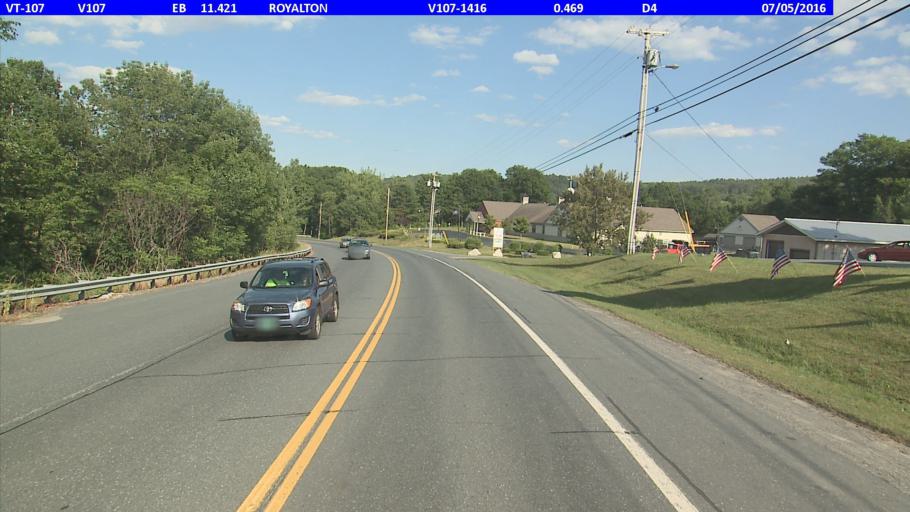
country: US
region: Vermont
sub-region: Orange County
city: Randolph
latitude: 43.8237
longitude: -72.6060
